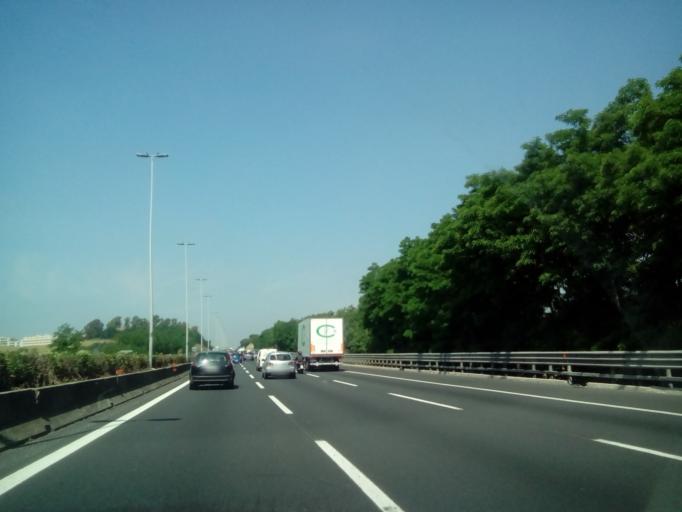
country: IT
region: Latium
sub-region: Citta metropolitana di Roma Capitale
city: Selcetta
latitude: 41.7947
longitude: 12.5064
